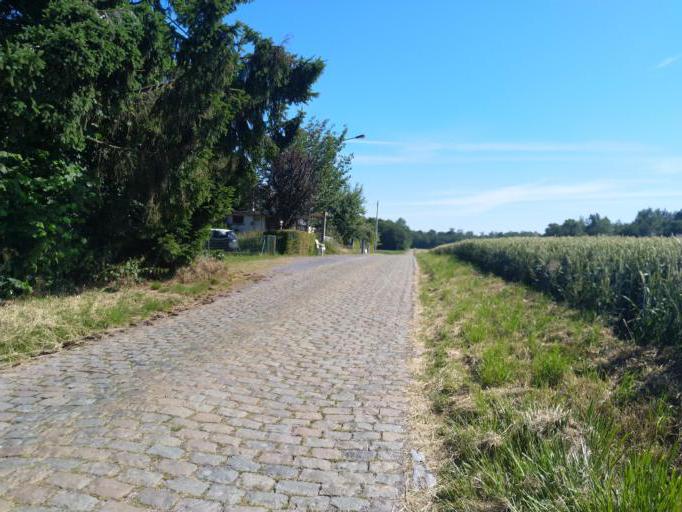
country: FR
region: Nord-Pas-de-Calais
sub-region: Departement du Nord
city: La Longueville
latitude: 50.3485
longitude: 3.8581
